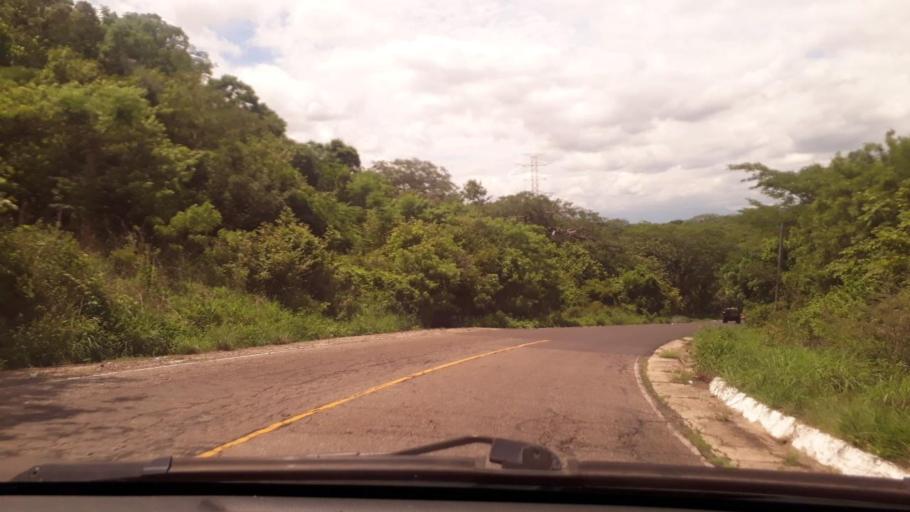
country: GT
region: Jutiapa
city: Jalpatagua
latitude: 14.1658
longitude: -90.0510
